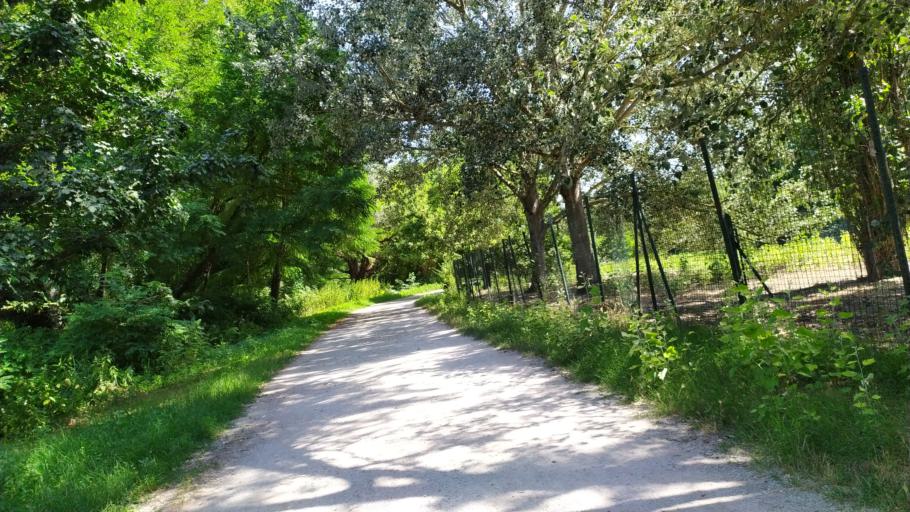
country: IT
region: Emilia-Romagna
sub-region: Forli-Cesena
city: Forli
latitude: 44.2179
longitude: 12.0294
